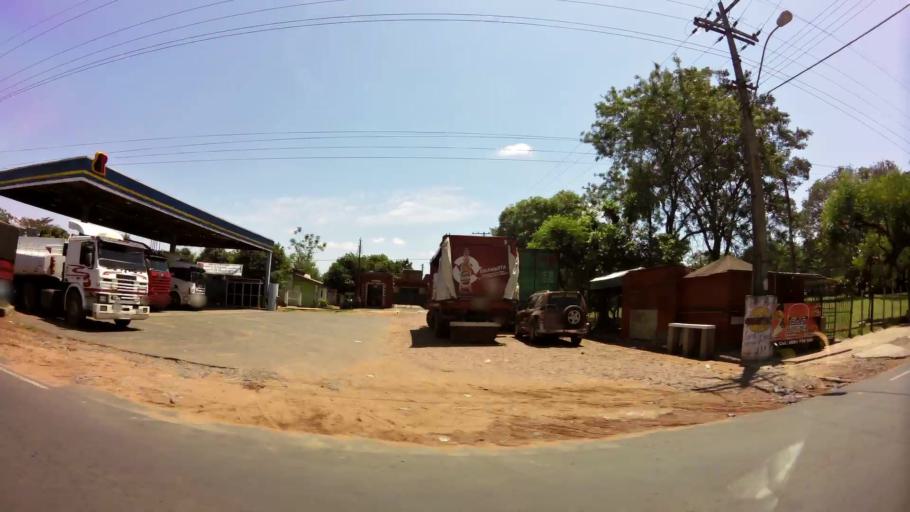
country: PY
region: Central
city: San Antonio
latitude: -25.4122
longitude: -57.5508
